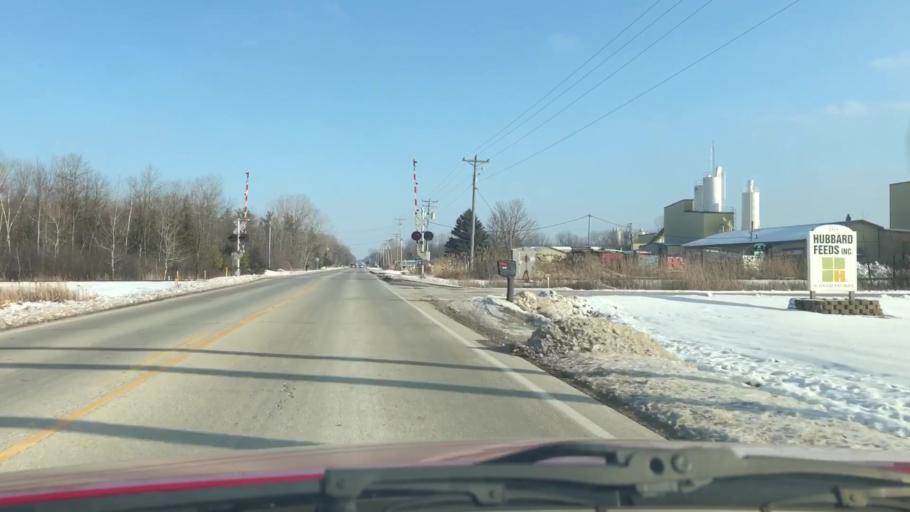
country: US
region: Wisconsin
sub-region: Outagamie County
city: Appleton
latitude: 44.3169
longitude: -88.4364
